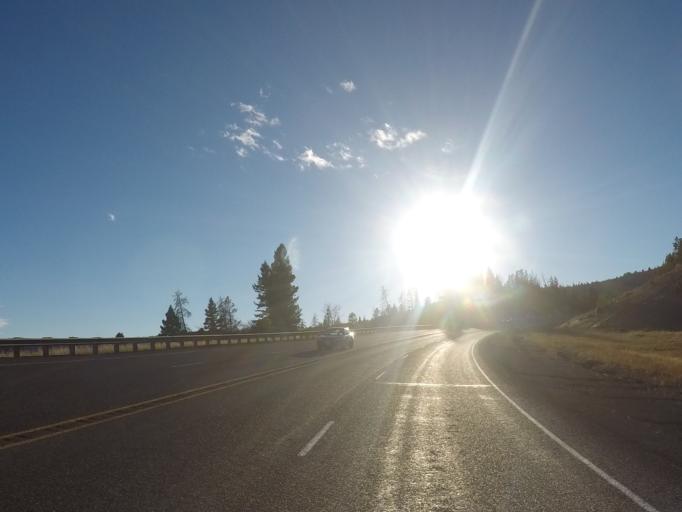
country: US
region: Montana
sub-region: Lewis and Clark County
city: Helena West Side
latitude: 46.5764
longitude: -112.2822
